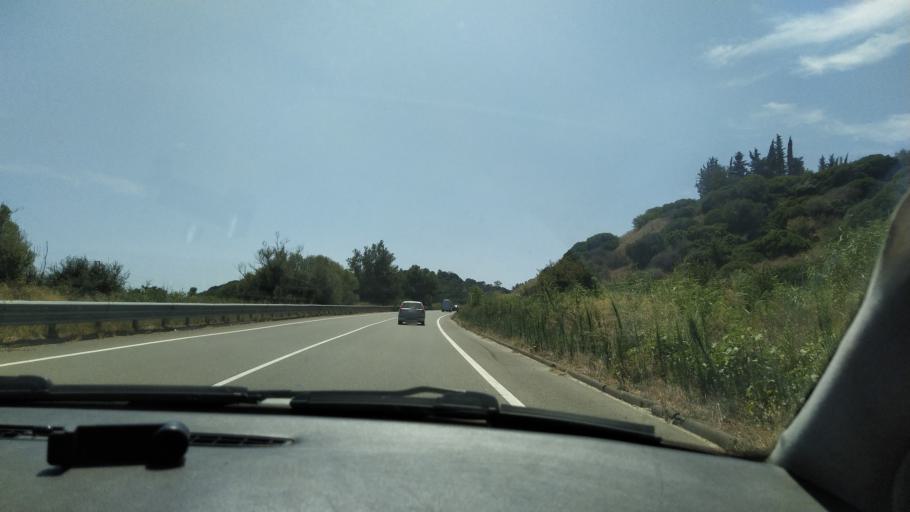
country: IT
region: Apulia
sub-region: Provincia di Taranto
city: Marina di Ginosa
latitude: 40.4319
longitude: 16.7925
